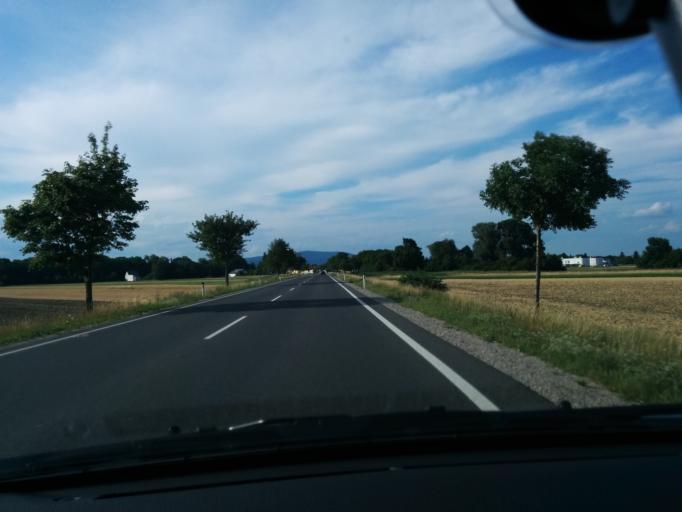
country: AT
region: Lower Austria
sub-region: Politischer Bezirk Baden
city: Schonau an der Triesting
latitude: 47.9330
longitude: 16.2630
